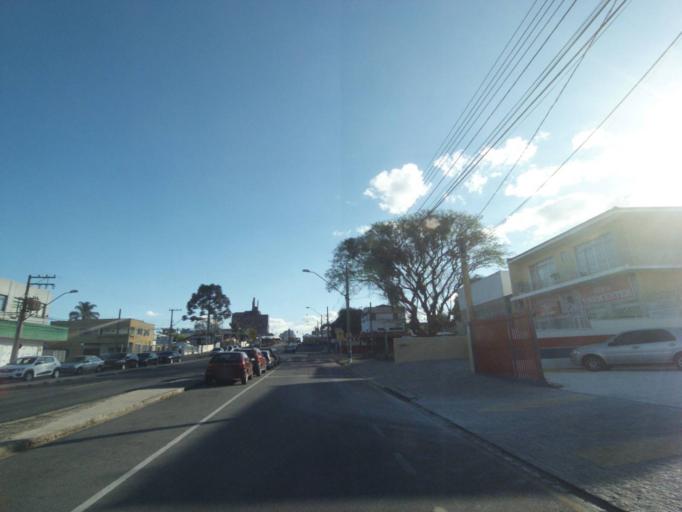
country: BR
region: Parana
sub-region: Curitiba
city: Curitiba
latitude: -25.3925
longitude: -49.2397
